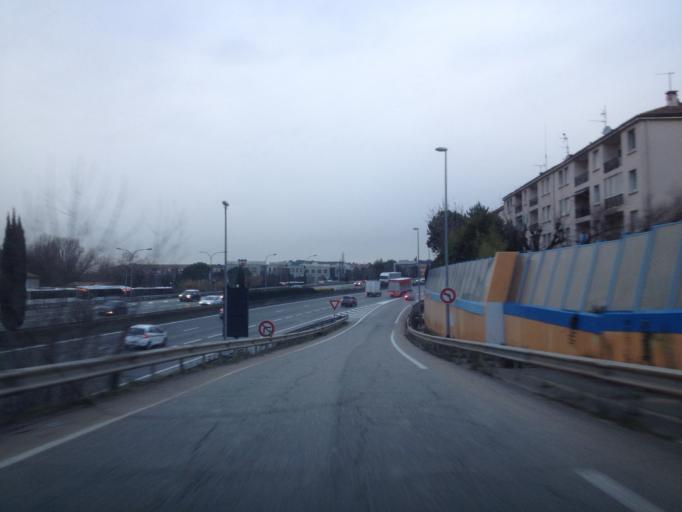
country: FR
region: Provence-Alpes-Cote d'Azur
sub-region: Departement des Bouches-du-Rhone
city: Aix-en-Provence
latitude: 43.5123
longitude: 5.4415
